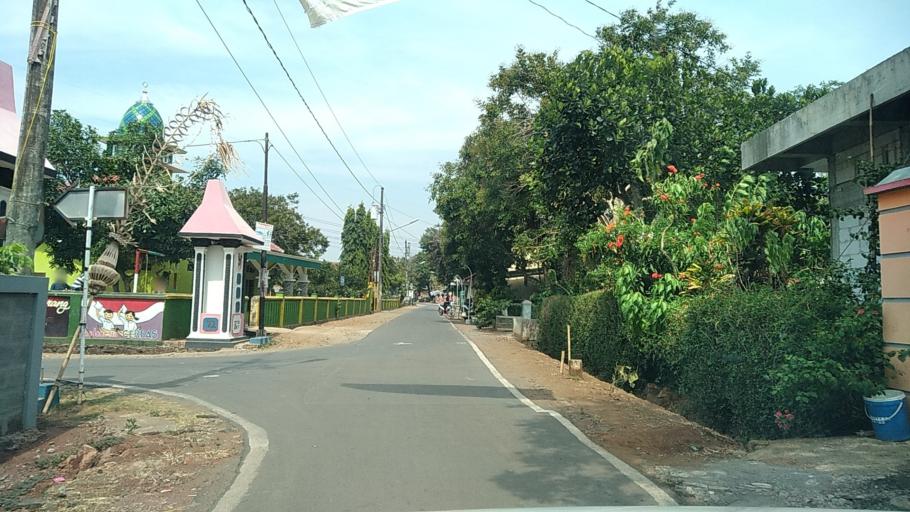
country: ID
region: Central Java
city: Ungaran
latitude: -7.0576
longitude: 110.3050
